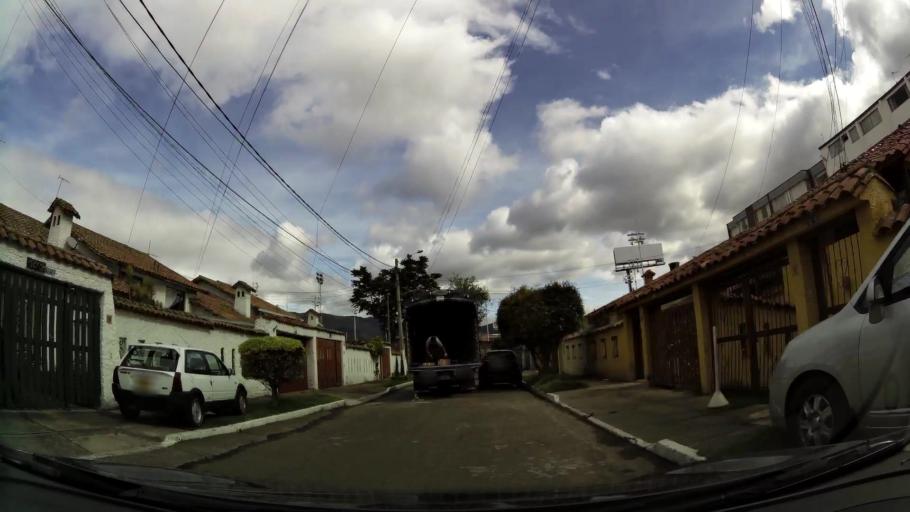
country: CO
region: Bogota D.C.
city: Barrio San Luis
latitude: 4.6917
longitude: -74.0654
